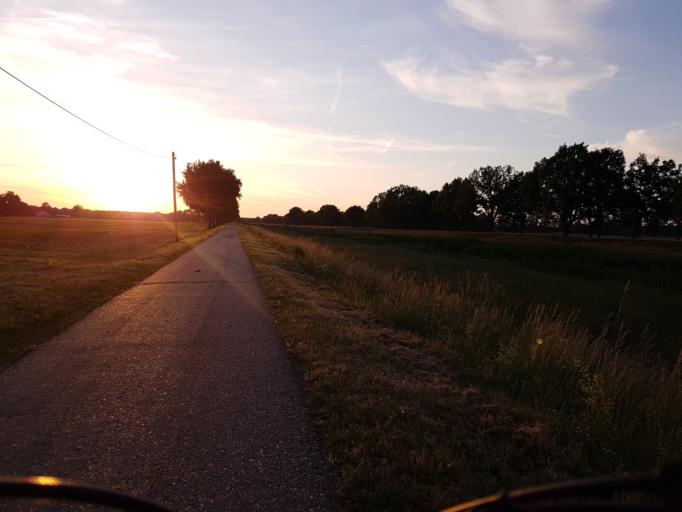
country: DE
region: Brandenburg
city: Falkenberg
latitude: 51.6105
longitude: 13.3038
